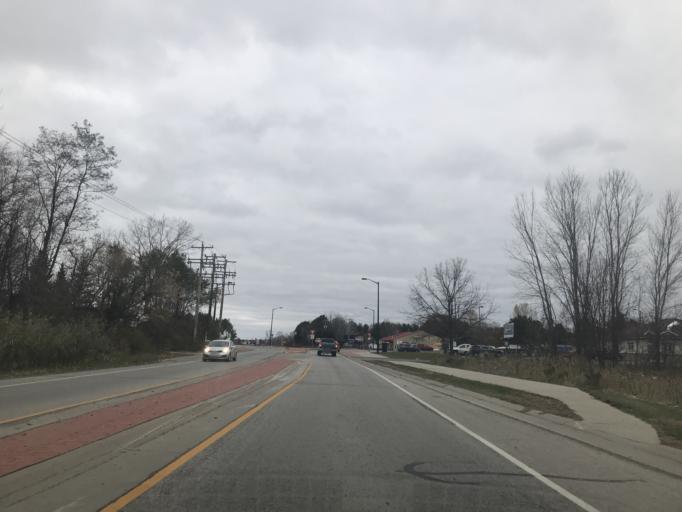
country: US
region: Wisconsin
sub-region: Marinette County
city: Marinette
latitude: 45.0986
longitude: -87.6603
